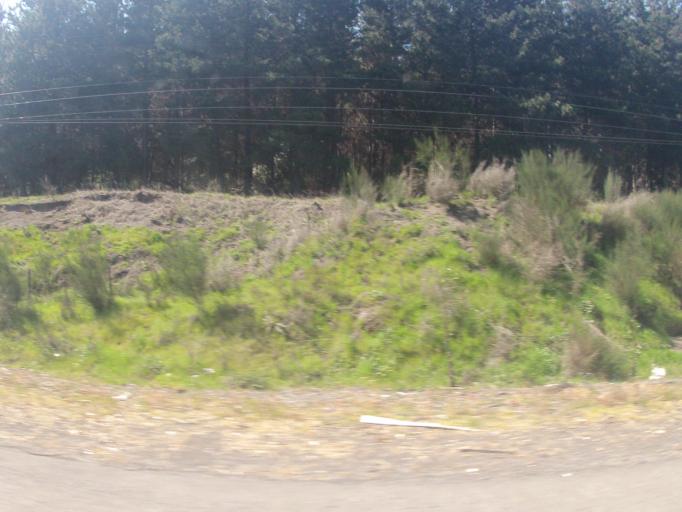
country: CL
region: Biobio
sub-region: Provincia de Biobio
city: Los Angeles
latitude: -37.3548
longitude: -72.3704
